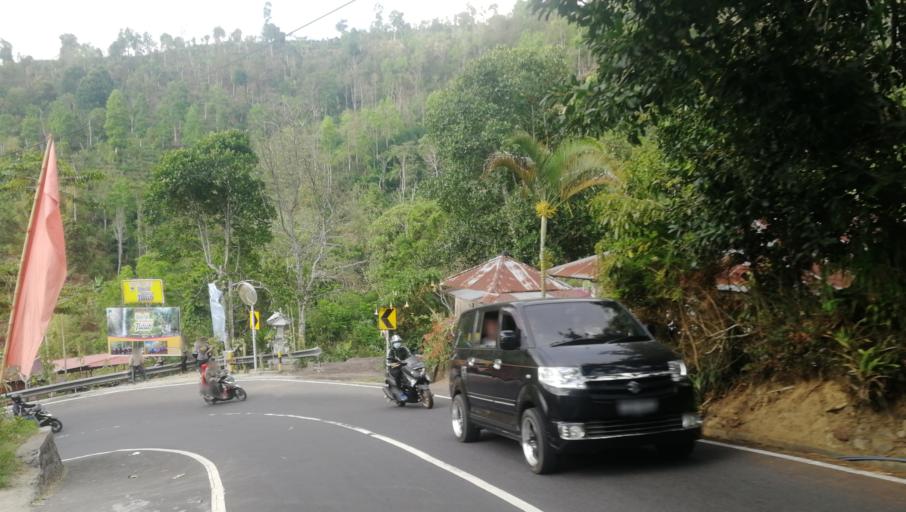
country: ID
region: Bali
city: Munduk
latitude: -8.2547
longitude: 115.0791
